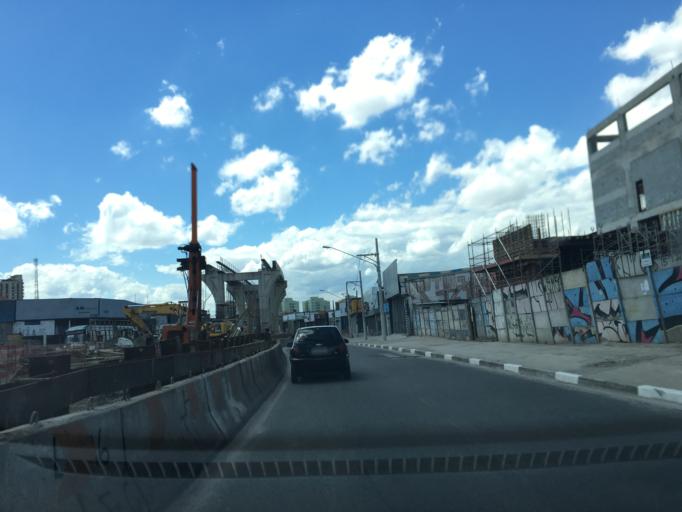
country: BR
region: Sao Paulo
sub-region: Sao Caetano Do Sul
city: Sao Caetano do Sul
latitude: -23.5893
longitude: -46.5442
